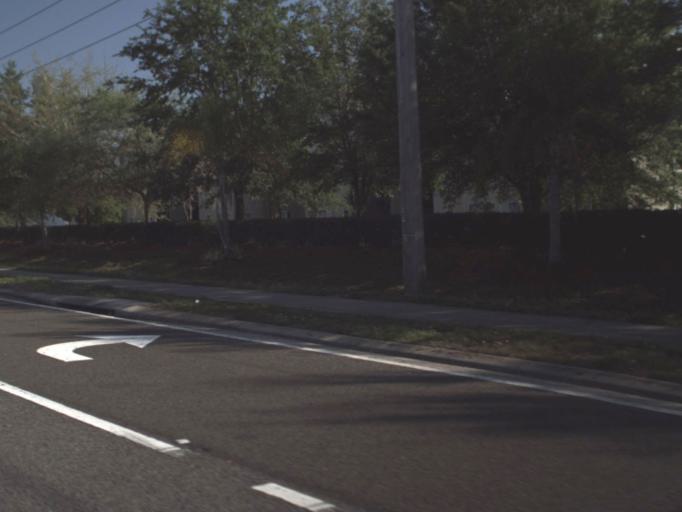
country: US
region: Florida
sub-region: Lake County
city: Four Corners
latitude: 28.3746
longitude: -81.6852
